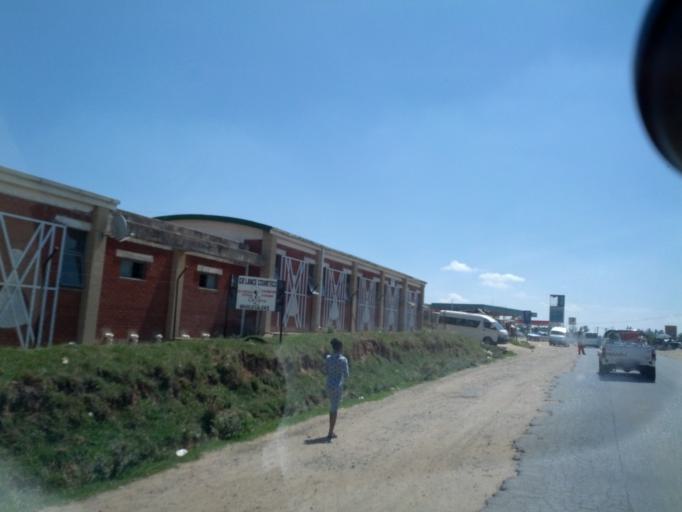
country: LS
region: Butha-Buthe
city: Butha-Buthe
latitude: -28.7693
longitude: 28.2483
